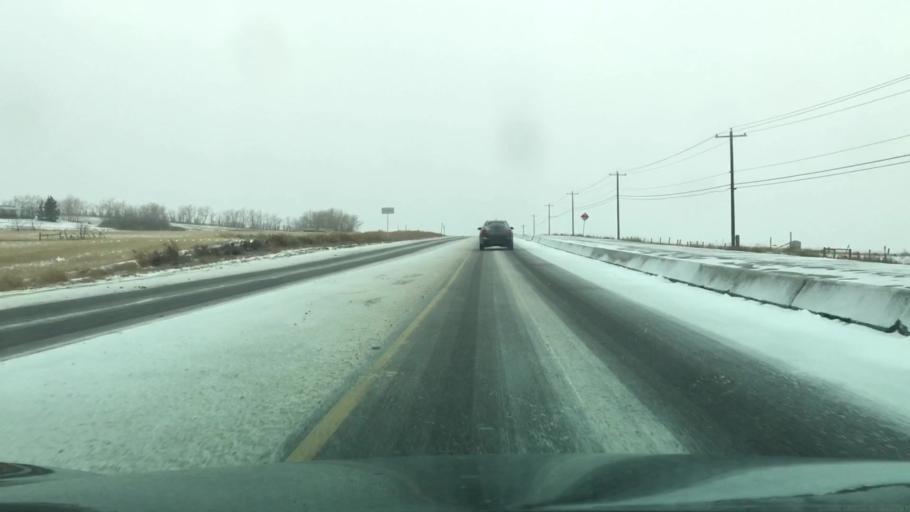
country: CA
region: Alberta
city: Calgary
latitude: 51.1831
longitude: -114.1778
